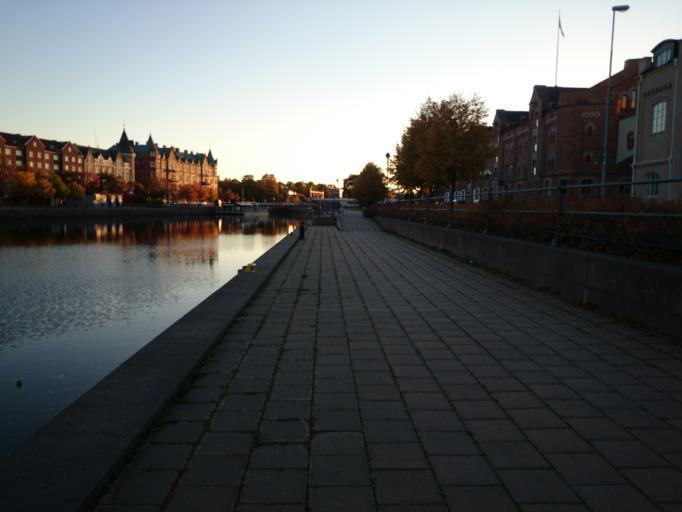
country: SE
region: Gaevleborg
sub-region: Gavle Kommun
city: Gavle
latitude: 60.6770
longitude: 17.1577
